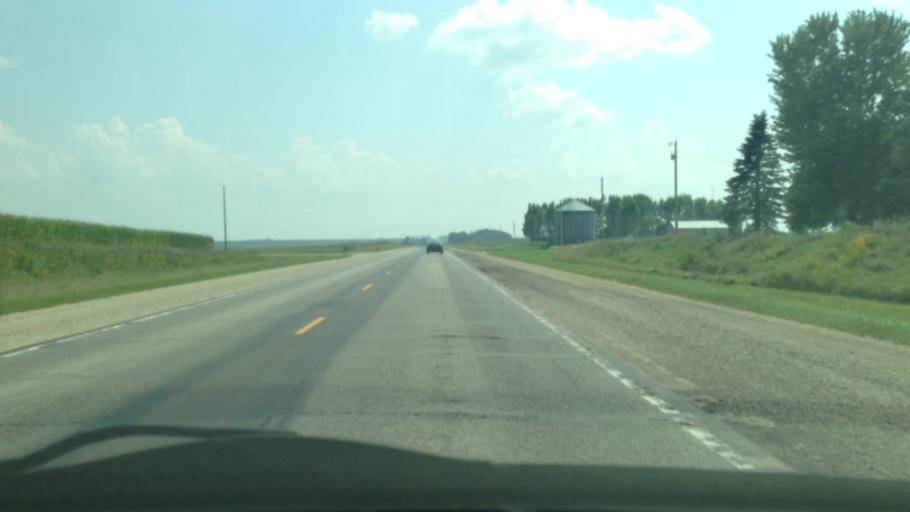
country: US
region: Iowa
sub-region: Howard County
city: Cresco
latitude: 43.3555
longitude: -92.2985
